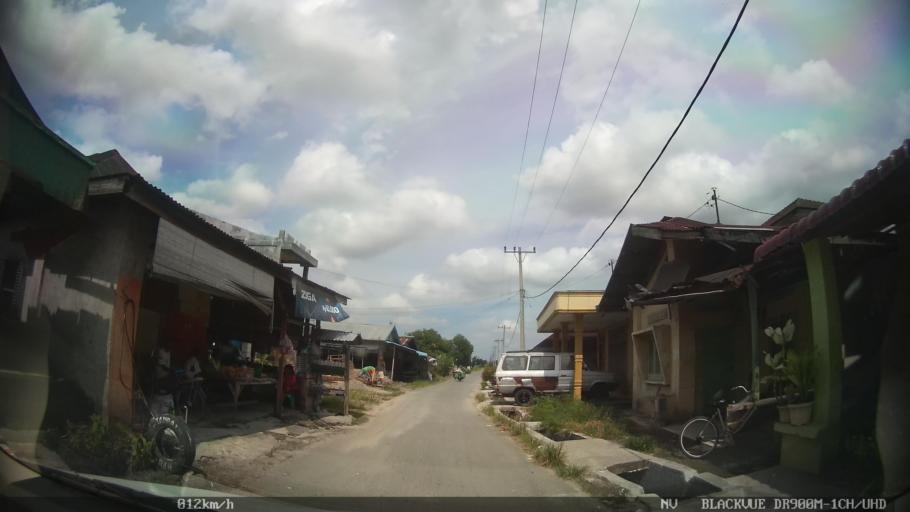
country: ID
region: North Sumatra
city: Percut
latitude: 3.5721
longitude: 98.8412
